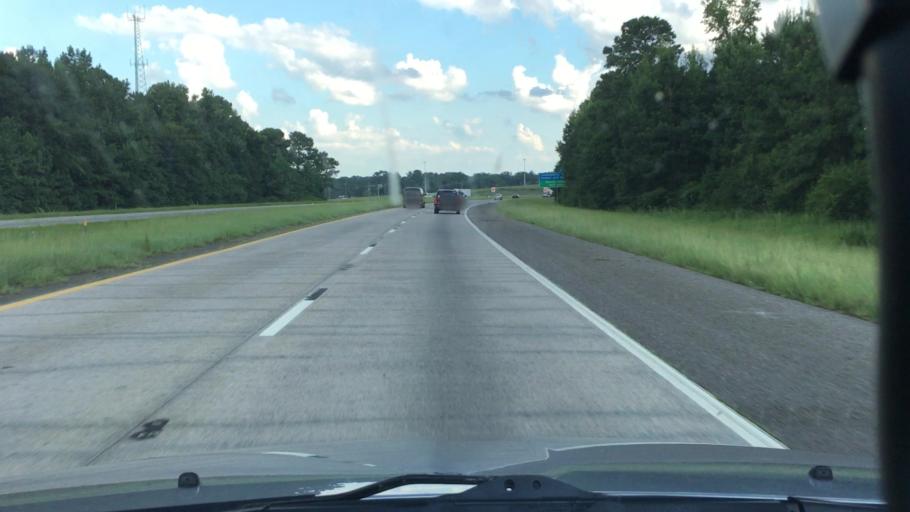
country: US
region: South Carolina
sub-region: Hampton County
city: Yemassee
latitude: 32.6376
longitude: -80.8823
